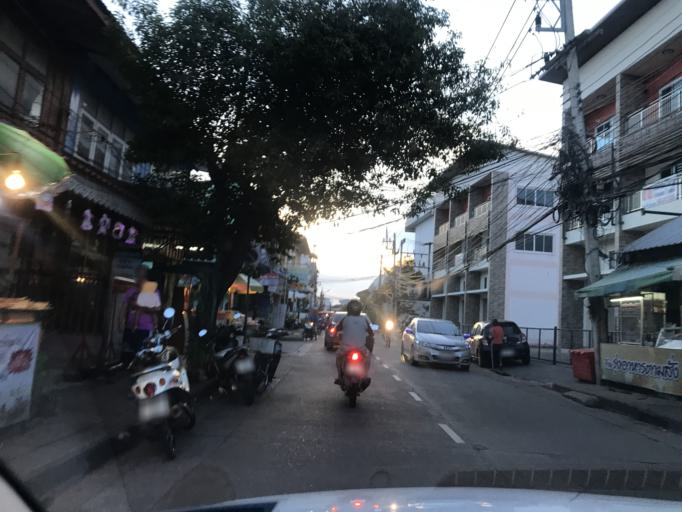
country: TH
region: Changwat Udon Thani
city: Udon Thani
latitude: 17.3950
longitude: 102.7917
